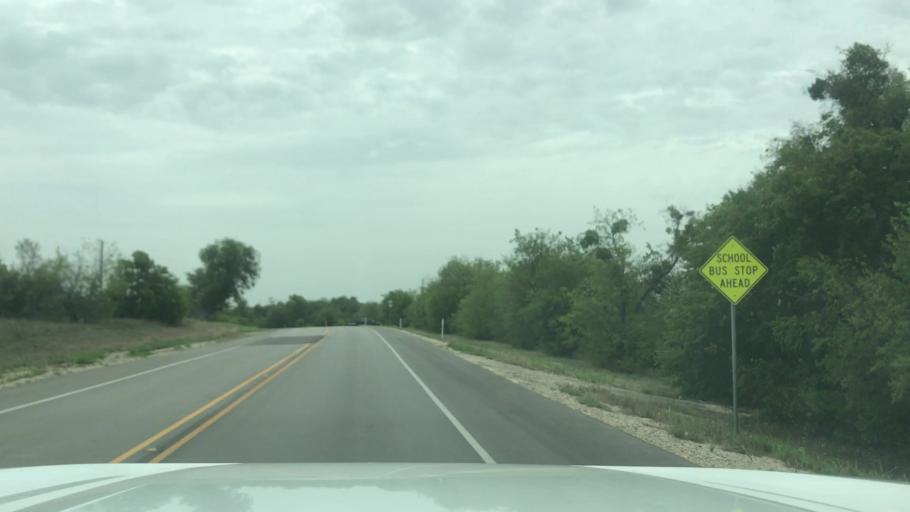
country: US
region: Texas
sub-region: Erath County
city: Dublin
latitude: 32.0613
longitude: -98.2124
